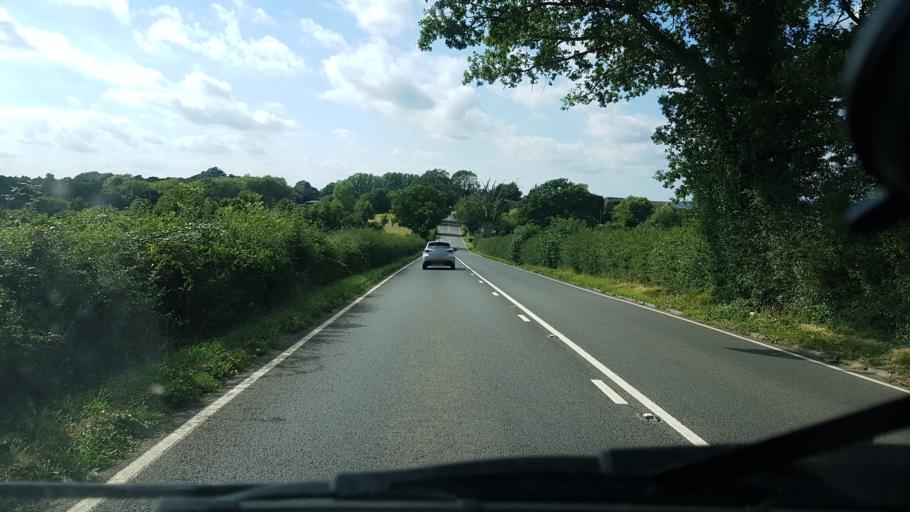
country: GB
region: England
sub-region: West Sussex
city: Rudgwick
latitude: 51.0984
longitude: -0.4934
